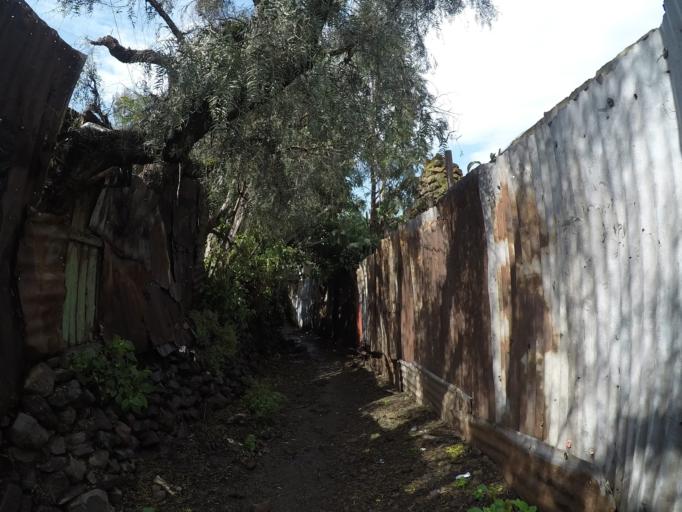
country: ET
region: Amhara
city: Lalibela
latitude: 12.0378
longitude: 39.0461
